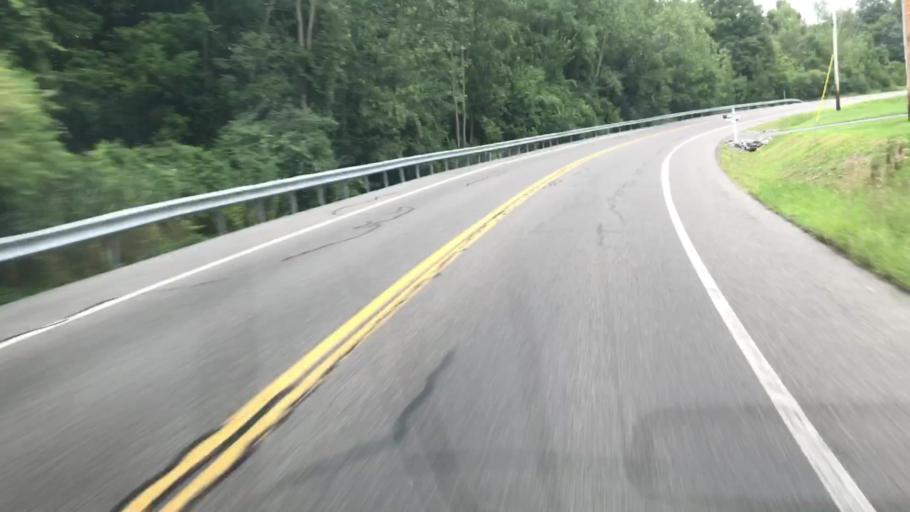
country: US
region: New York
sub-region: Onondaga County
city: Camillus
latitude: 43.0729
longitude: -76.3268
